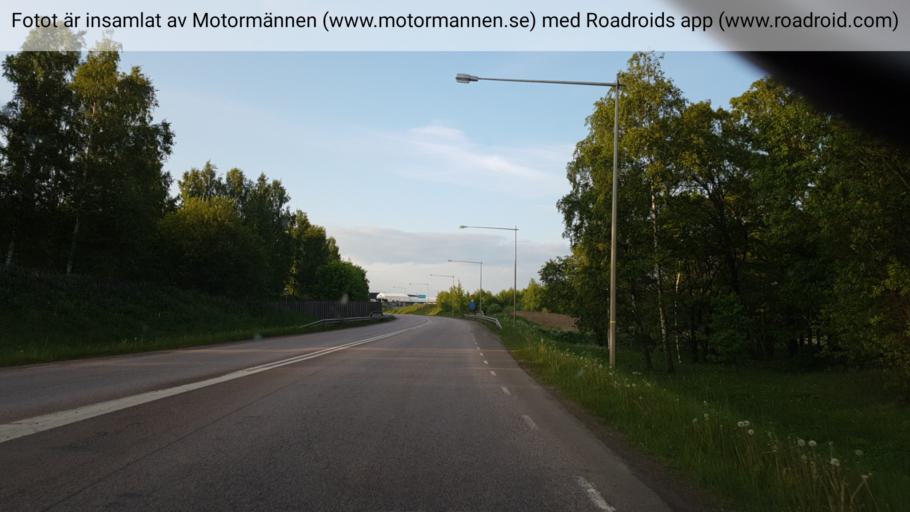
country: SE
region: Vaestra Goetaland
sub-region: Skovde Kommun
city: Skoevde
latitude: 58.3822
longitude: 13.8728
